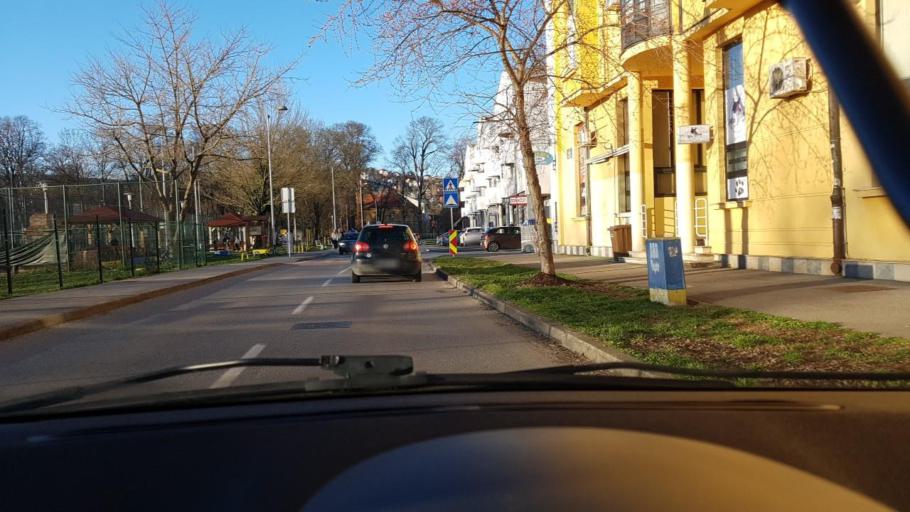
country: HR
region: Grad Zagreb
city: Stenjevec
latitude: 45.8136
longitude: 15.8984
